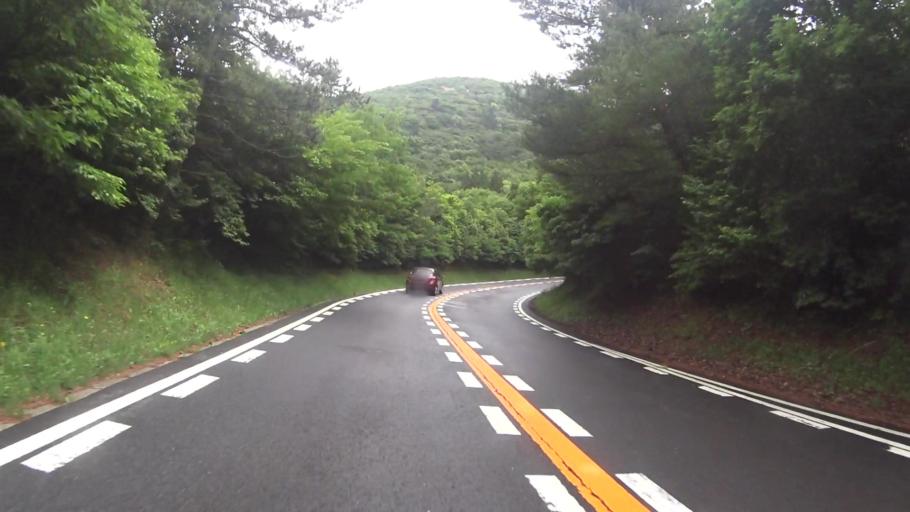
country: JP
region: Oita
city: Tsukawaki
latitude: 33.1028
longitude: 131.2223
